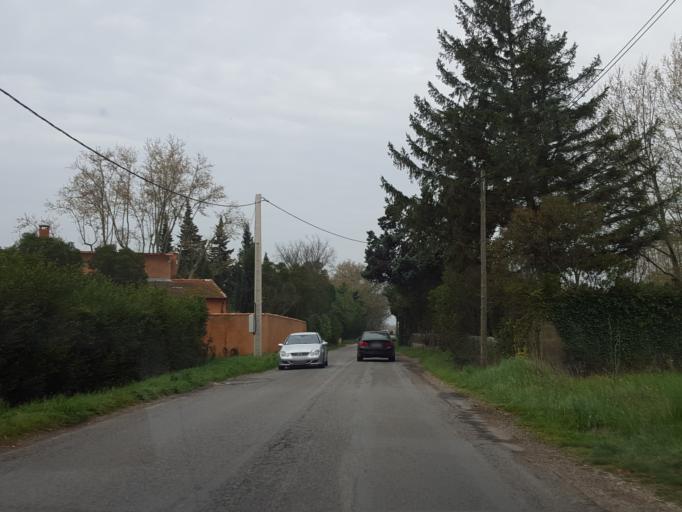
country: FR
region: Provence-Alpes-Cote d'Azur
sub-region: Departement du Vaucluse
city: Morieres-les-Avignon
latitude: 43.9225
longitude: 4.9006
